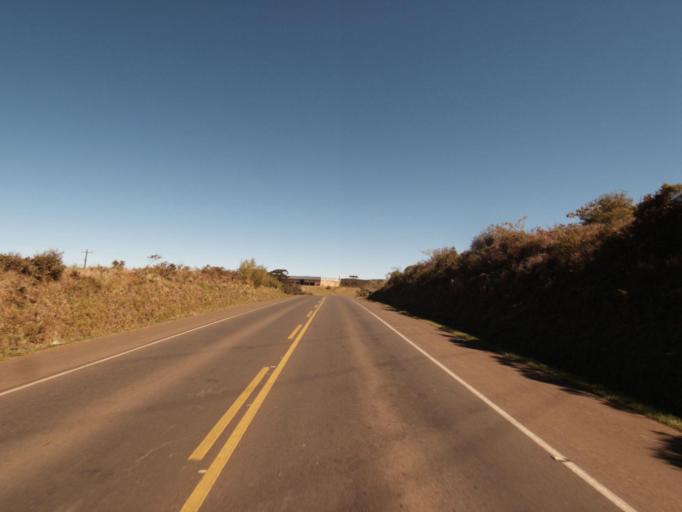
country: BR
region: Santa Catarina
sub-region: Concordia
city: Concordia
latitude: -26.9172
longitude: -51.9246
